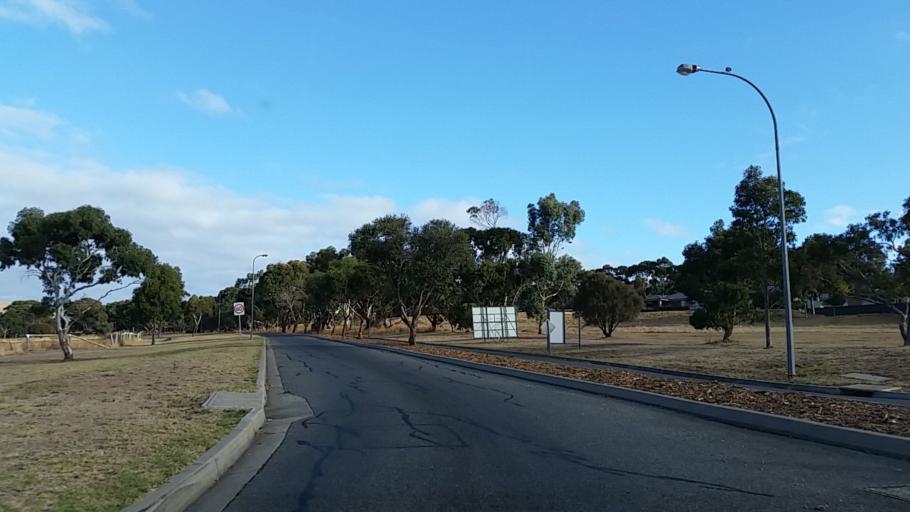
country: AU
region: South Australia
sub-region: Yankalilla
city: Normanville
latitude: -35.5027
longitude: 138.2559
